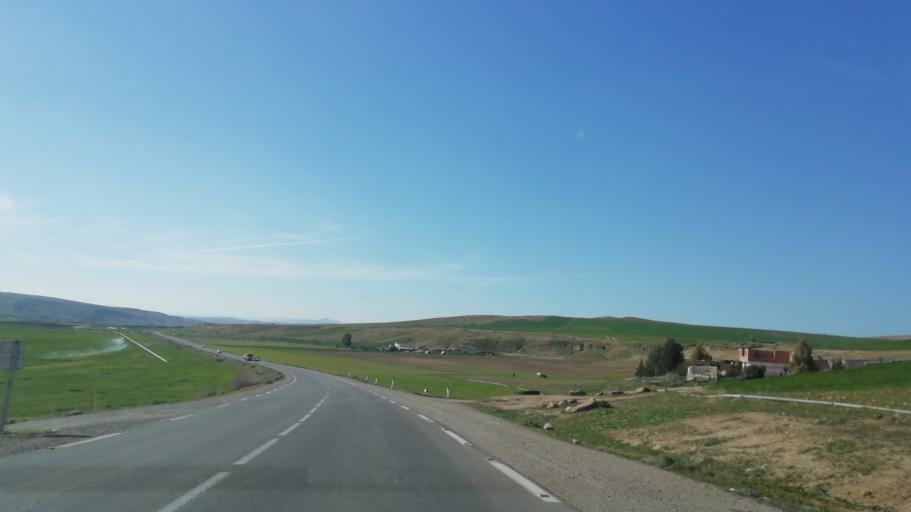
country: DZ
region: Mascara
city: Oued el Abtal
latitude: 35.4494
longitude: 0.8067
